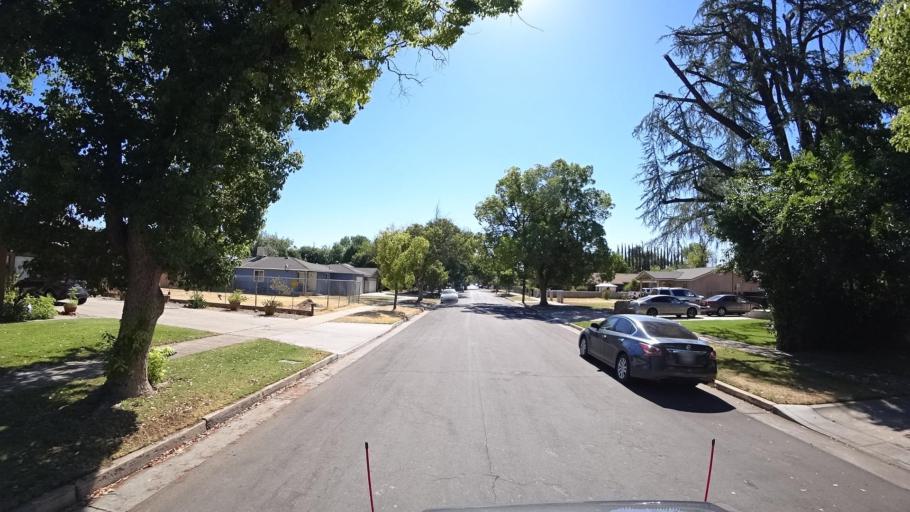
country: US
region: California
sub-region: Fresno County
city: Fresno
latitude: 36.7813
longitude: -119.7989
